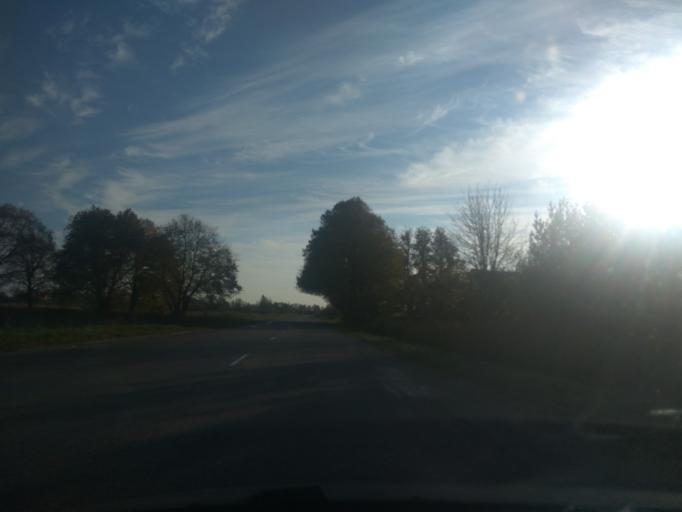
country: LV
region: Ventspils
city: Ventspils
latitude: 57.3320
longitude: 21.5638
